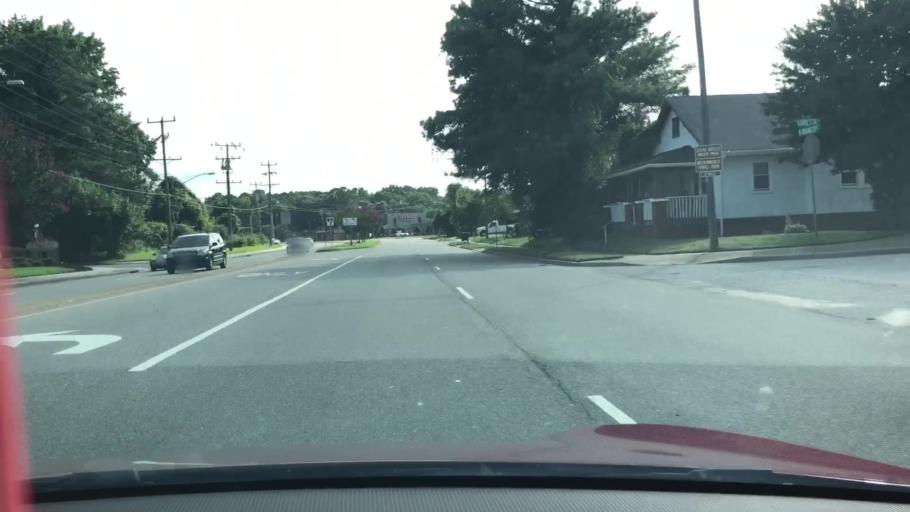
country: US
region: Virginia
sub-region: City of Virginia Beach
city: Virginia Beach
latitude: 36.8403
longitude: -75.9969
